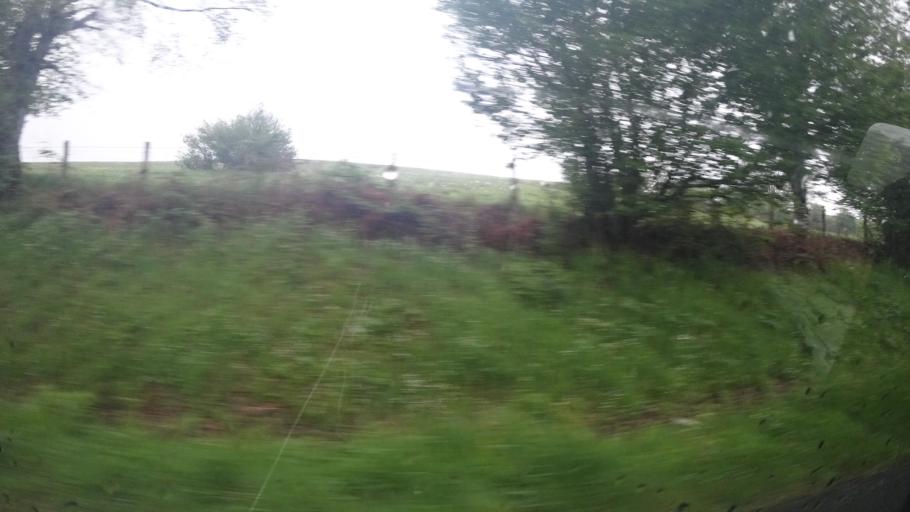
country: FR
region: Midi-Pyrenees
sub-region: Departement de l'Aveyron
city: Laissac
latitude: 44.3214
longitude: 2.7957
